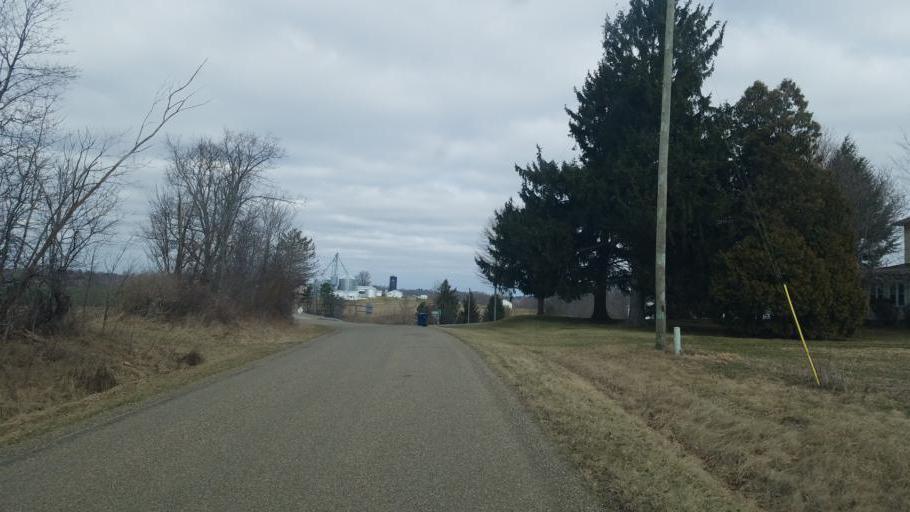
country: US
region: Ohio
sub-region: Richland County
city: Mansfield
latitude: 40.7014
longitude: -82.4969
